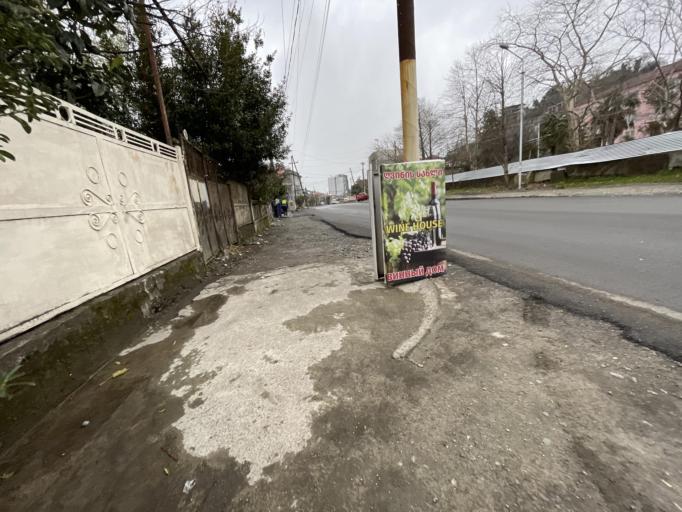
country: GE
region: Ajaria
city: Batumi
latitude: 41.6352
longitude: 41.6453
